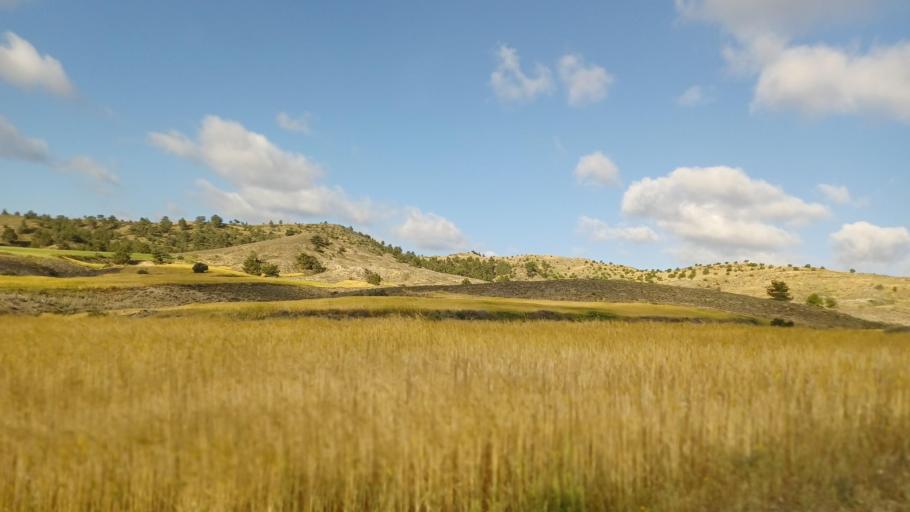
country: CY
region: Lefkosia
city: Peristerona
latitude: 35.0718
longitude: 33.0449
